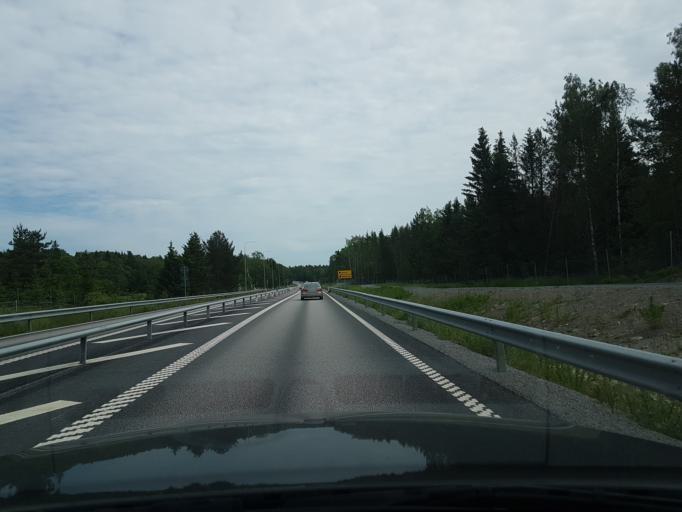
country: SE
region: Stockholm
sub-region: Norrtalje Kommun
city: Bjorko
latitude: 59.7213
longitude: 18.9108
